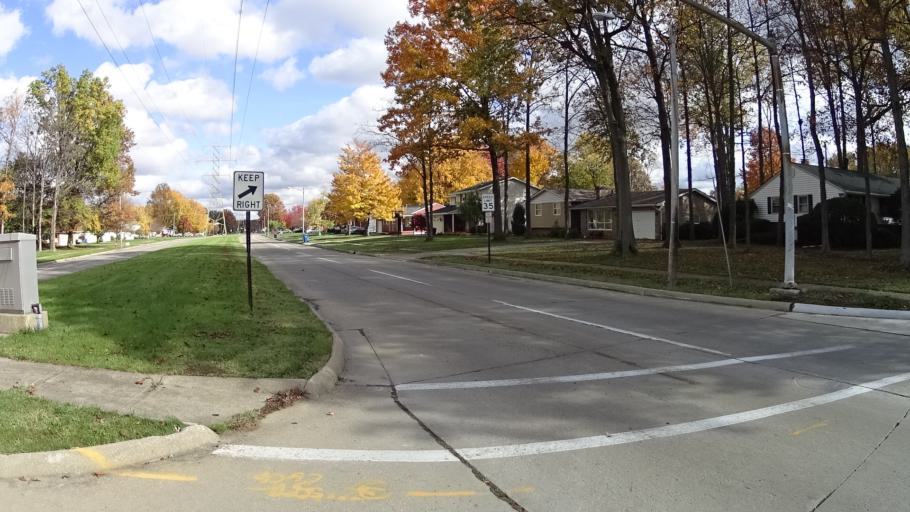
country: US
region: Ohio
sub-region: Lorain County
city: Lorain
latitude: 41.4320
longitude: -82.1933
